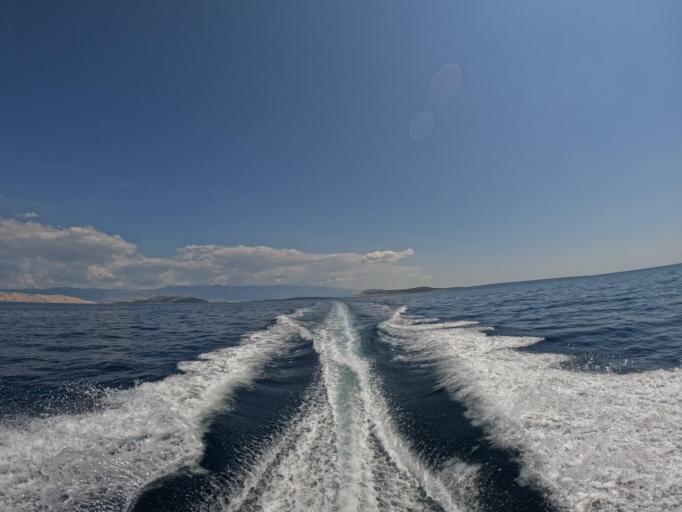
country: HR
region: Primorsko-Goranska
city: Lopar
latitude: 44.8811
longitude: 14.6503
